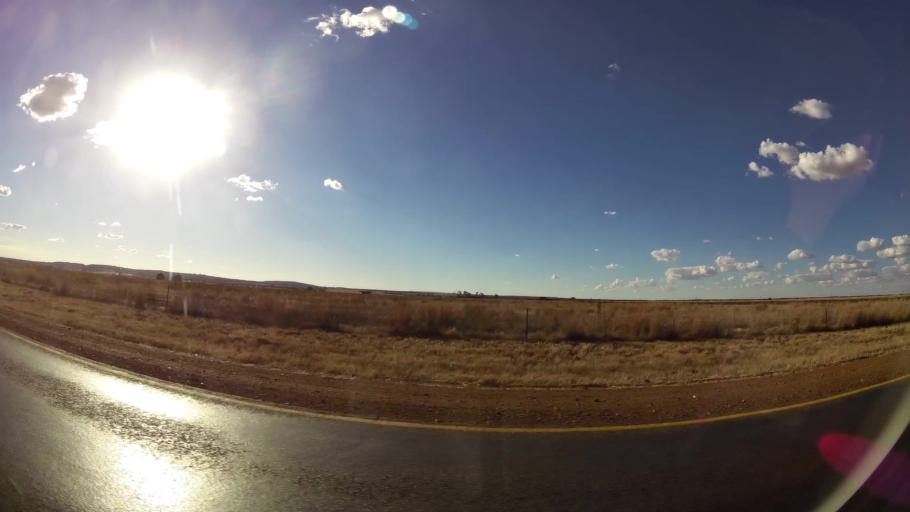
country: ZA
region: North-West
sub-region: Dr Kenneth Kaunda District Municipality
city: Stilfontein
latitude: -26.8446
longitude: 26.7287
